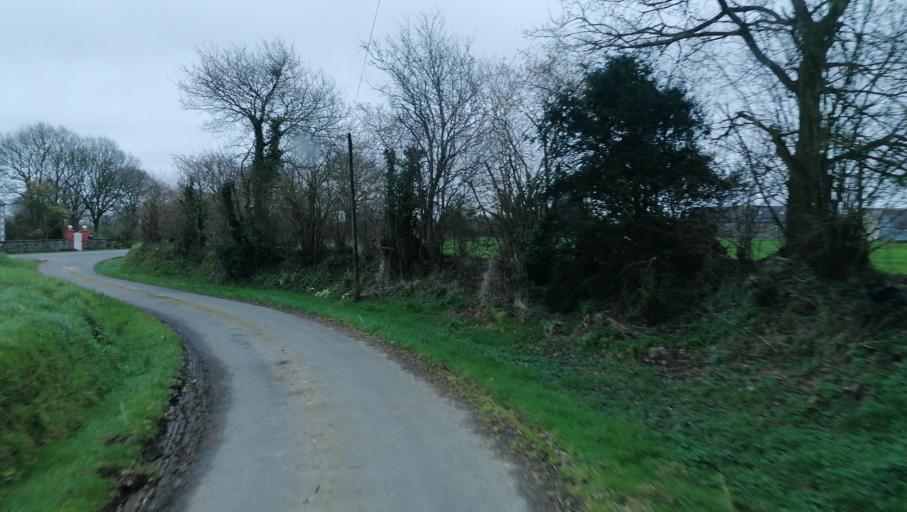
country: FR
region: Brittany
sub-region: Departement des Cotes-d'Armor
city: Saint-Agathon
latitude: 48.5648
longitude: -3.0584
